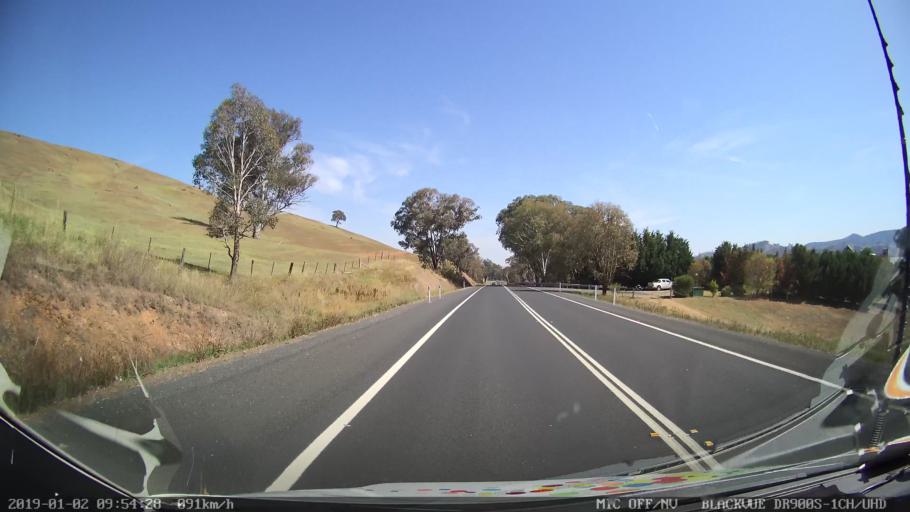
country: AU
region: New South Wales
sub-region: Tumut Shire
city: Tumut
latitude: -35.2346
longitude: 148.1960
